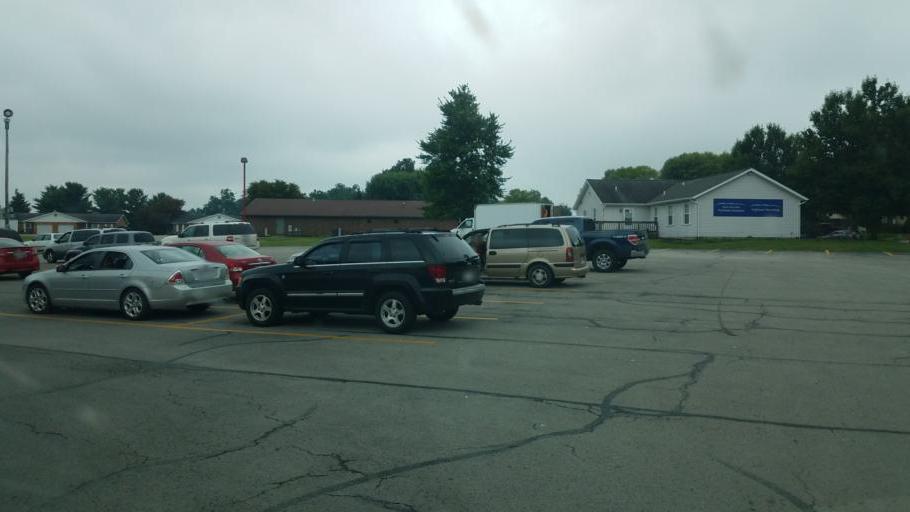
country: US
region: Ohio
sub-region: Highland County
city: Hillsboro
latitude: 39.2241
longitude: -83.6100
